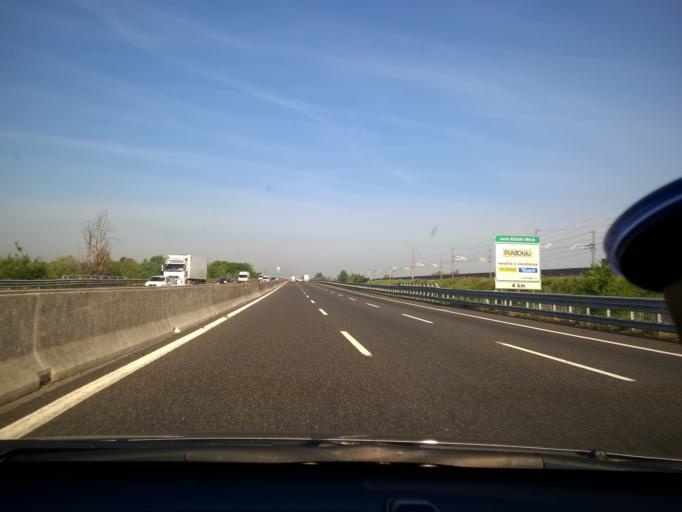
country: IT
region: Emilia-Romagna
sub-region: Provincia di Reggio Emilia
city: Massenzatico
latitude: 44.7188
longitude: 10.6789
